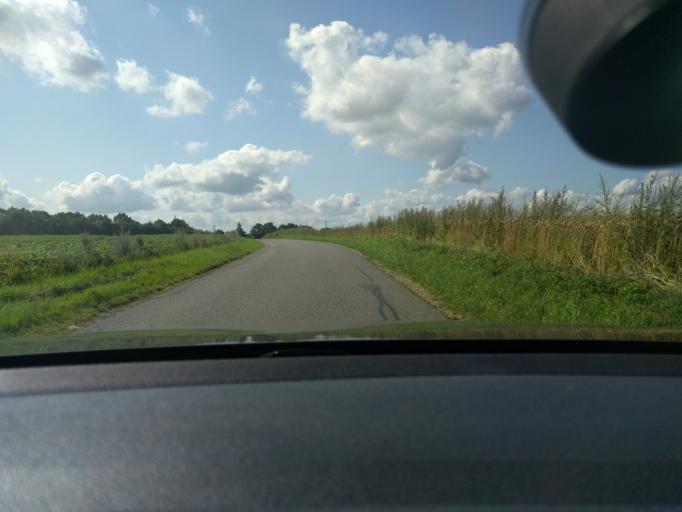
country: DK
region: Central Jutland
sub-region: Viborg Kommune
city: Viborg
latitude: 56.5054
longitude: 9.5063
